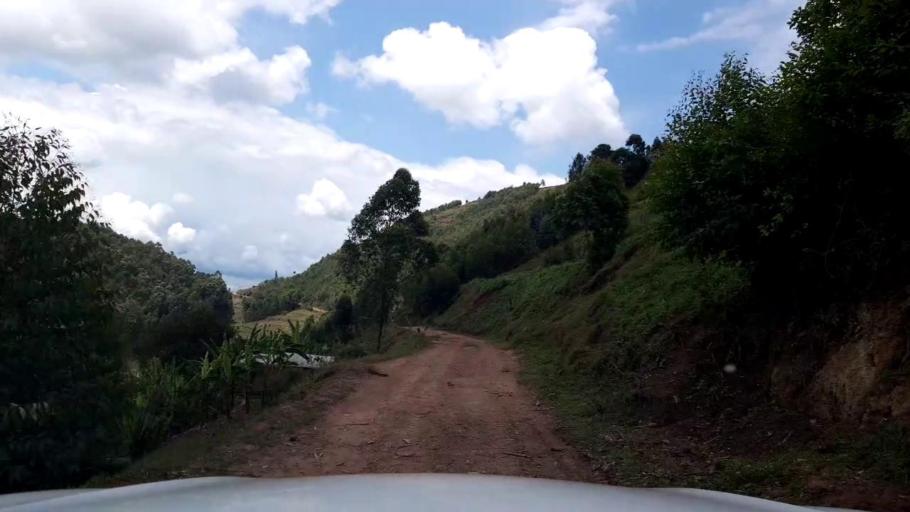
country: RW
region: Northern Province
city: Byumba
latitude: -1.5259
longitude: 30.1309
